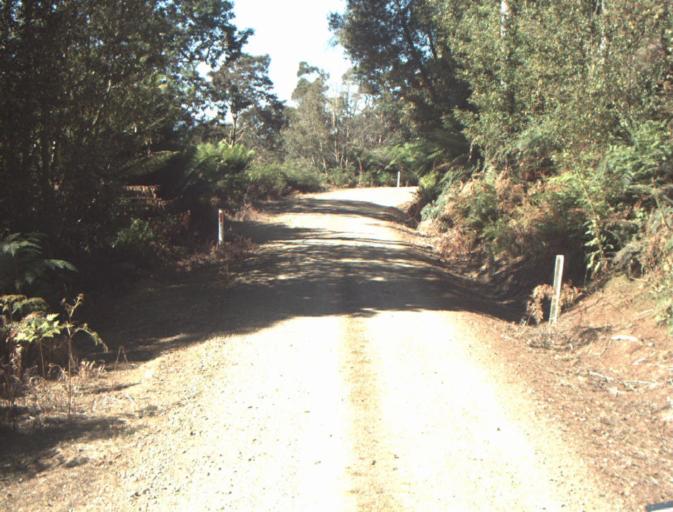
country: AU
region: Tasmania
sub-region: Dorset
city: Scottsdale
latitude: -41.2729
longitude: 147.3636
